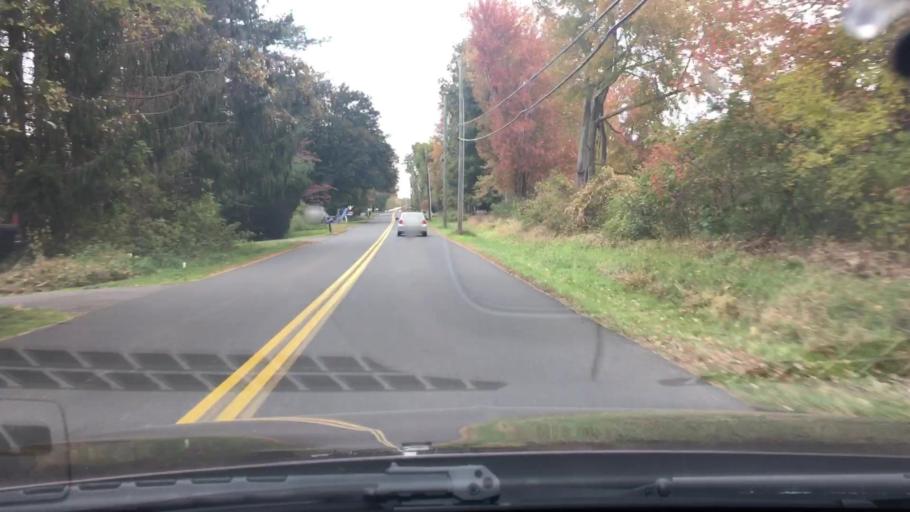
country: US
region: Connecticut
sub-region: Tolland County
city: Ellington
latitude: 41.9327
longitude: -72.4780
